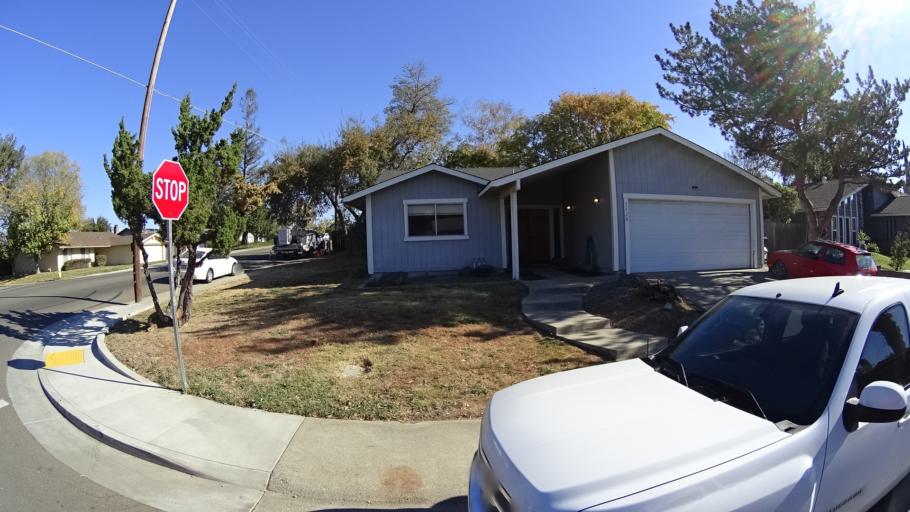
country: US
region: California
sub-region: Sacramento County
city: Citrus Heights
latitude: 38.7219
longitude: -121.2989
